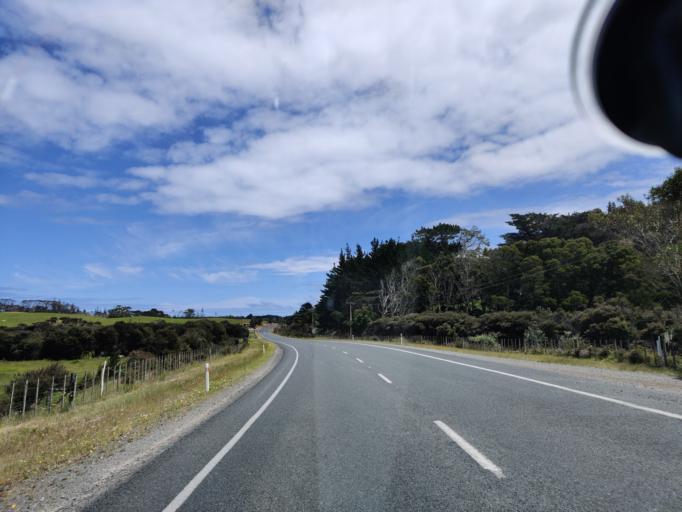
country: NZ
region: Northland
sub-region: Far North District
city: Kaitaia
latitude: -35.0134
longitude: 173.2111
